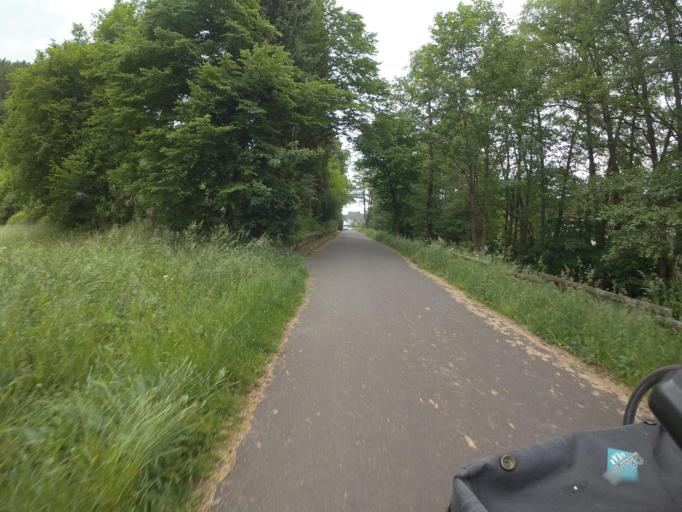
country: DE
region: North Rhine-Westphalia
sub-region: Regierungsbezirk Koln
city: Hellenthal
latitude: 50.4952
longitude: 6.4584
